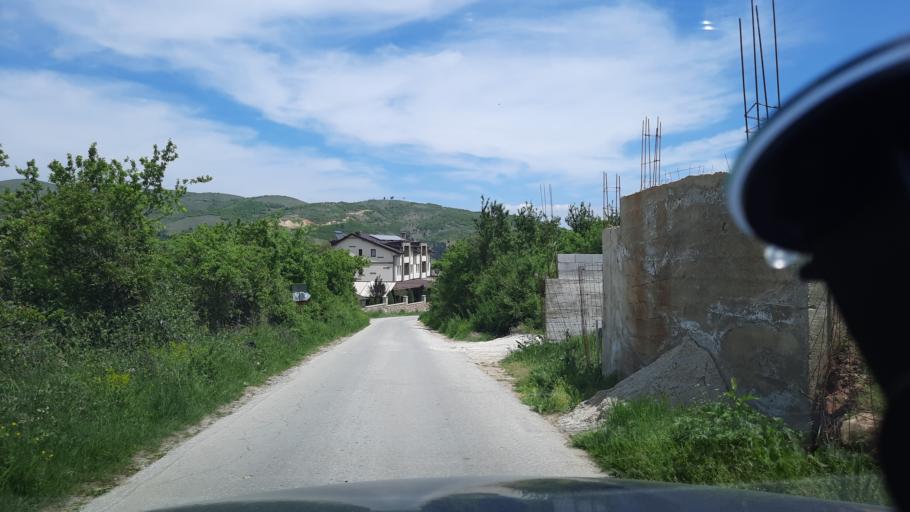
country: MK
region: Bitola
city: Bitola
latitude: 41.0312
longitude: 21.2919
